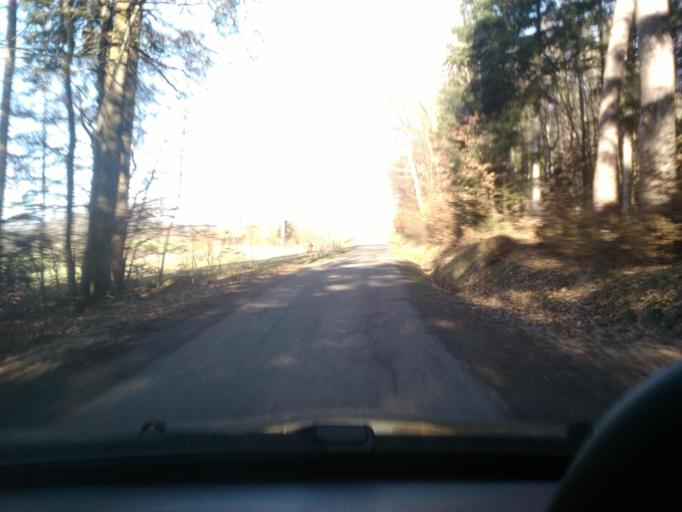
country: FR
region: Lorraine
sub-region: Departement des Vosges
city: Moyenmoutier
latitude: 48.3585
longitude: 6.9248
